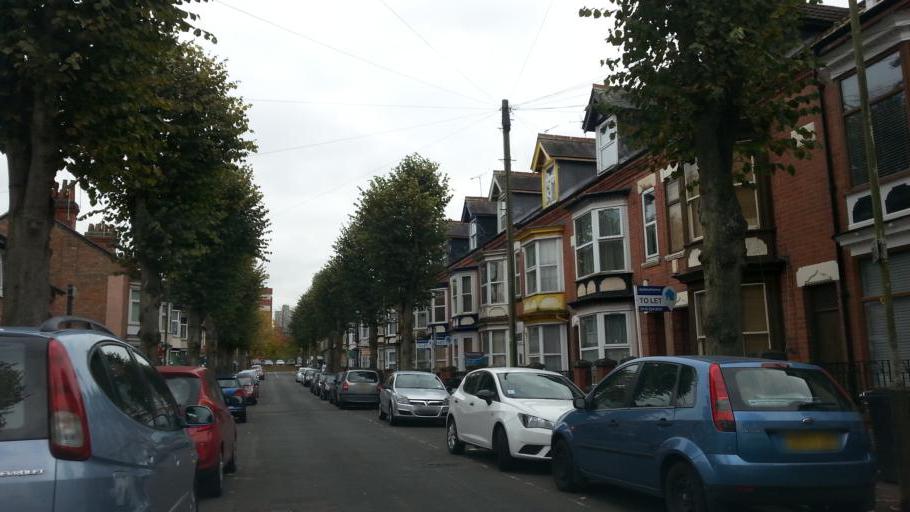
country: GB
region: England
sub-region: City of Leicester
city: Leicester
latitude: 52.6226
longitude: -1.1373
